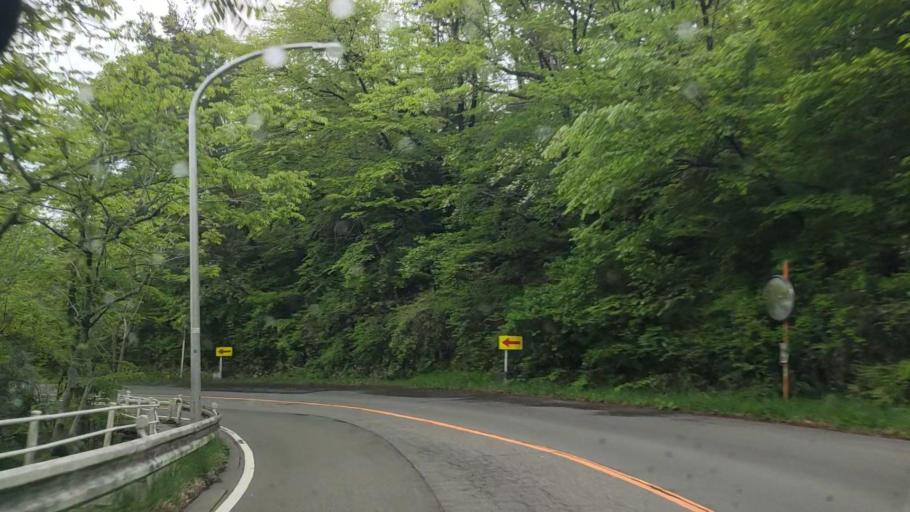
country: JP
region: Miyagi
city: Sendai
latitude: 38.2572
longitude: 140.8482
